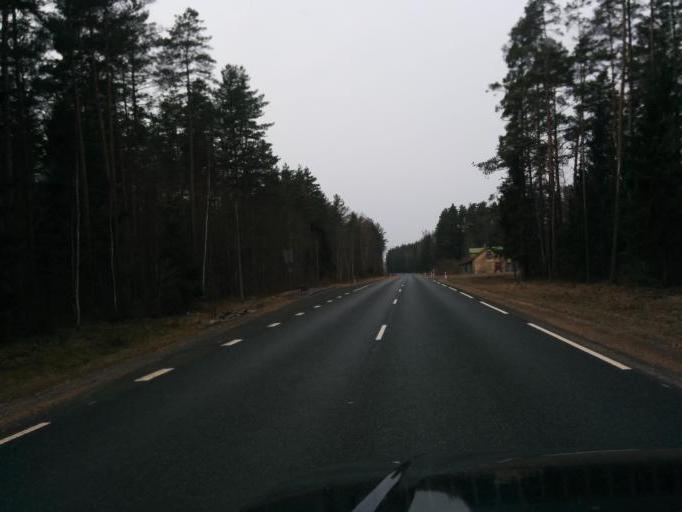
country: LV
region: Ogre
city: Ogre
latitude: 56.8025
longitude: 24.5792
